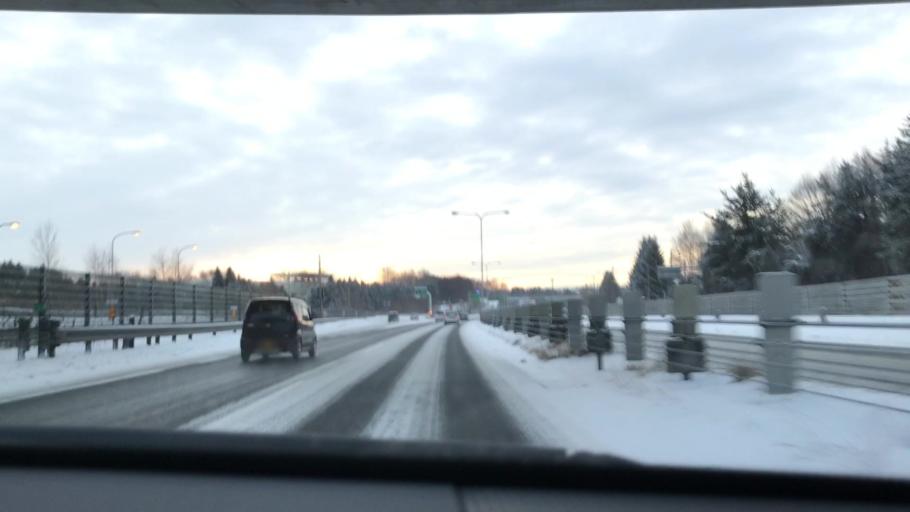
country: JP
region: Hokkaido
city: Kitahiroshima
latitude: 43.0209
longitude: 141.4594
